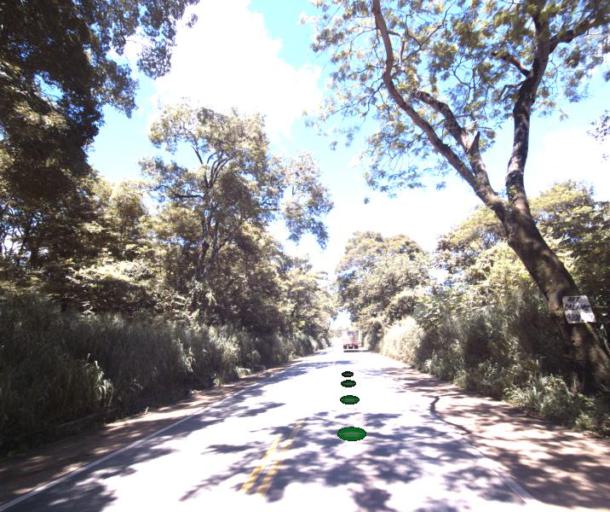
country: BR
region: Goias
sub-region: Anapolis
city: Anapolis
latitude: -16.1327
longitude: -49.0474
